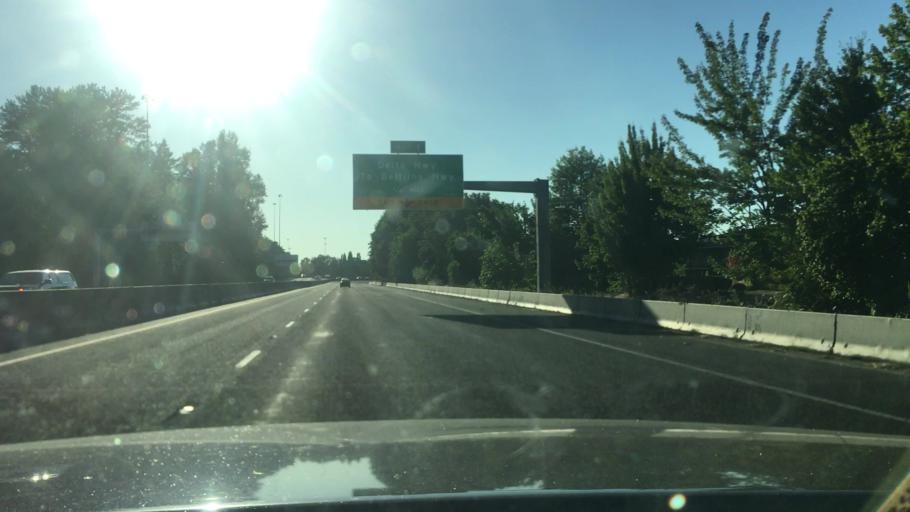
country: US
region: Oregon
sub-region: Lane County
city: Eugene
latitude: 44.0620
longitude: -123.0901
